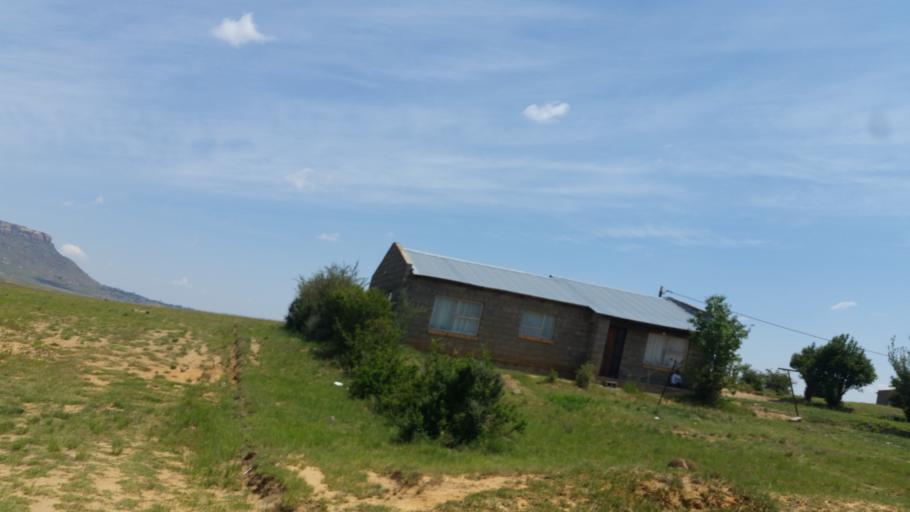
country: LS
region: Mafeteng
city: Mafeteng
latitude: -29.7082
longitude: 27.4282
